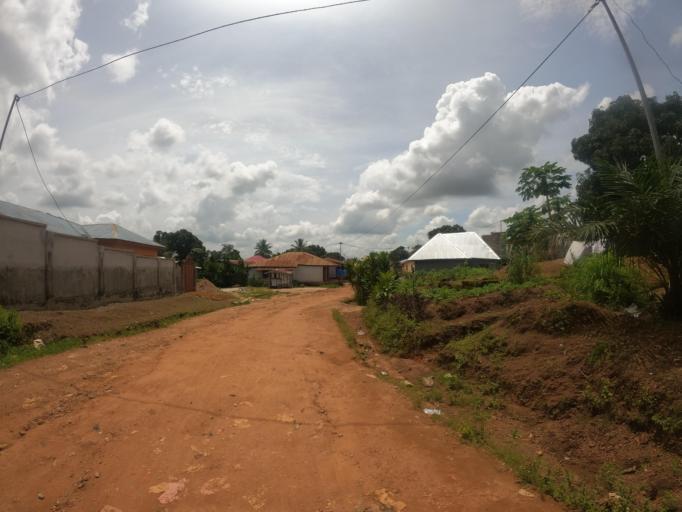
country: SL
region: Northern Province
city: Makeni
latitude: 8.8966
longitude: -12.0511
